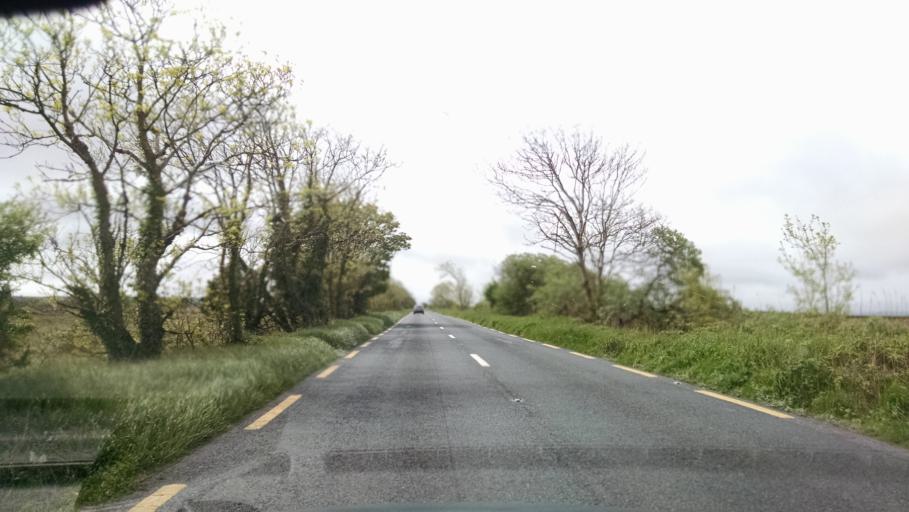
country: IE
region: Connaught
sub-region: County Galway
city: Claregalway
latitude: 53.3563
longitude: -9.0179
